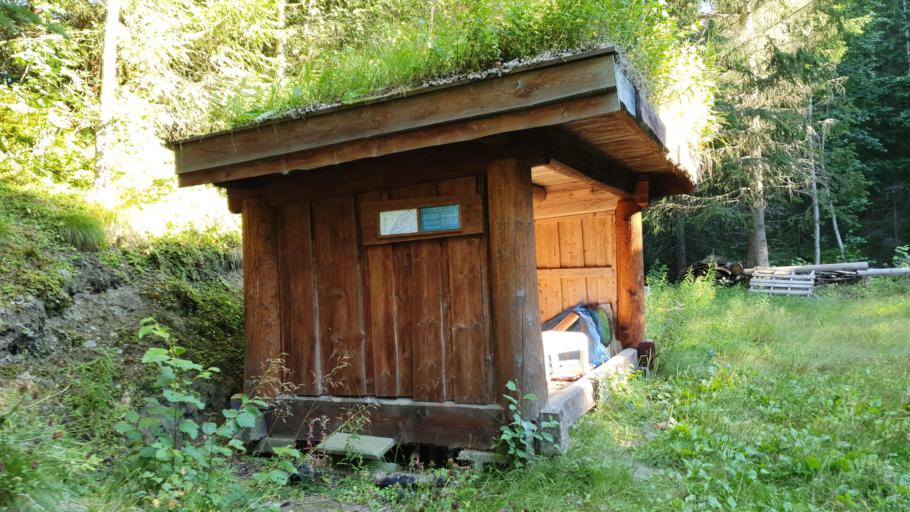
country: NO
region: Nord-Trondelag
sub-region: Levanger
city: Levanger
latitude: 63.6958
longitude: 11.2775
